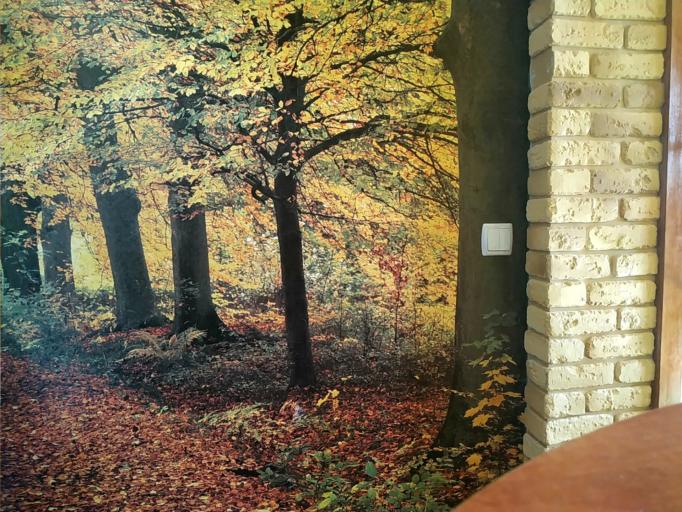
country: RU
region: Jaroslavl
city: Kukoboy
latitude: 58.8514
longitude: 39.7371
